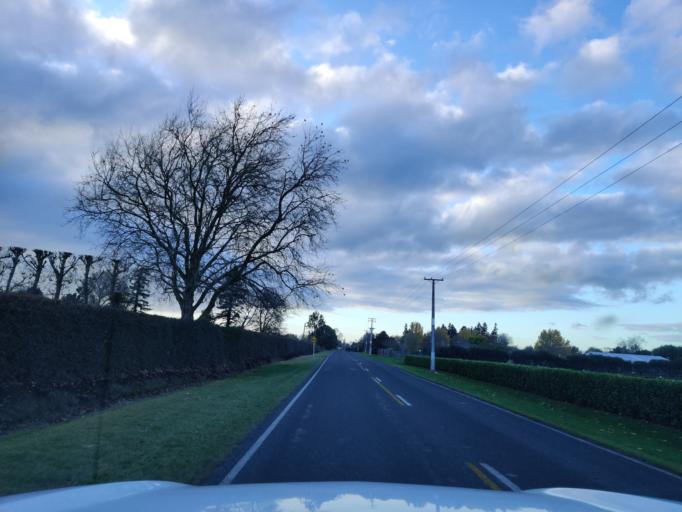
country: NZ
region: Waikato
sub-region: Waipa District
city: Cambridge
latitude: -37.8562
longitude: 175.4390
